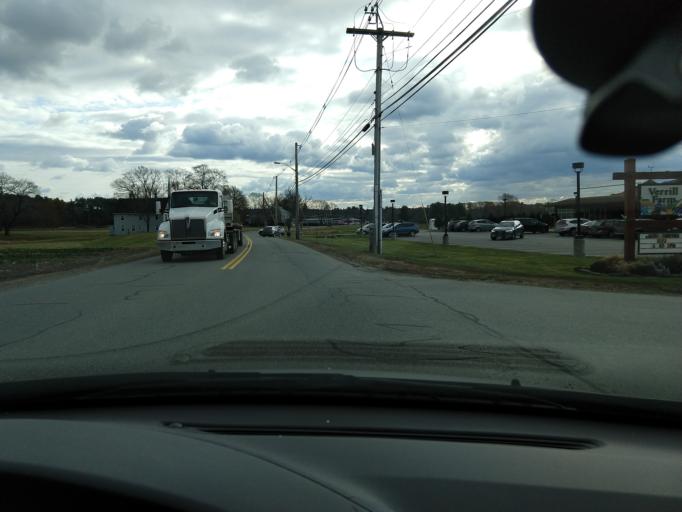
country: US
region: Massachusetts
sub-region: Middlesex County
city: West Concord
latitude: 42.4252
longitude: -71.3741
